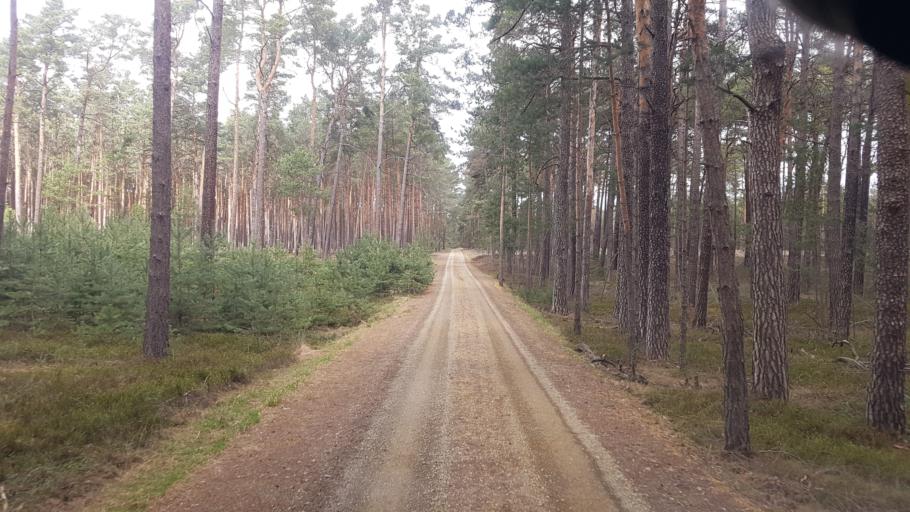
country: DE
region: Brandenburg
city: Schonborn
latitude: 51.6538
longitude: 13.4962
